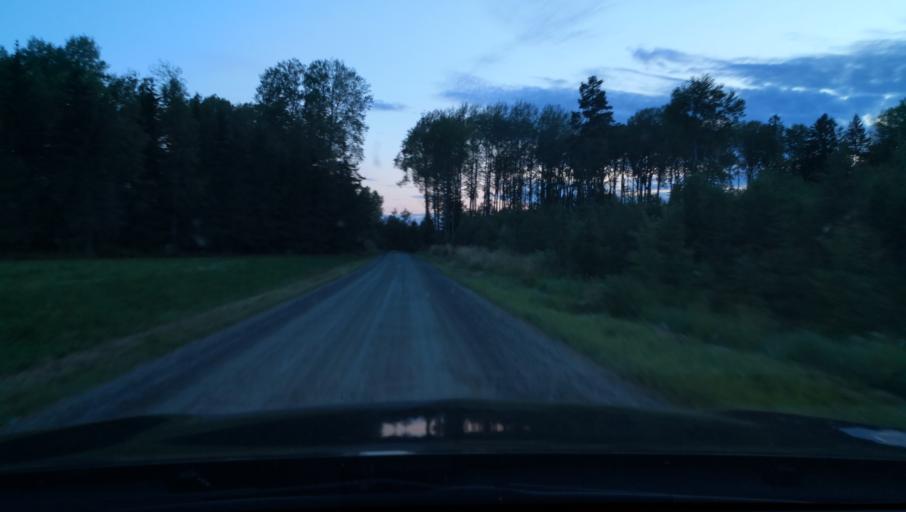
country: SE
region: Uppsala
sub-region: Osthammars Kommun
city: Bjorklinge
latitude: 60.0034
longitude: 17.3466
